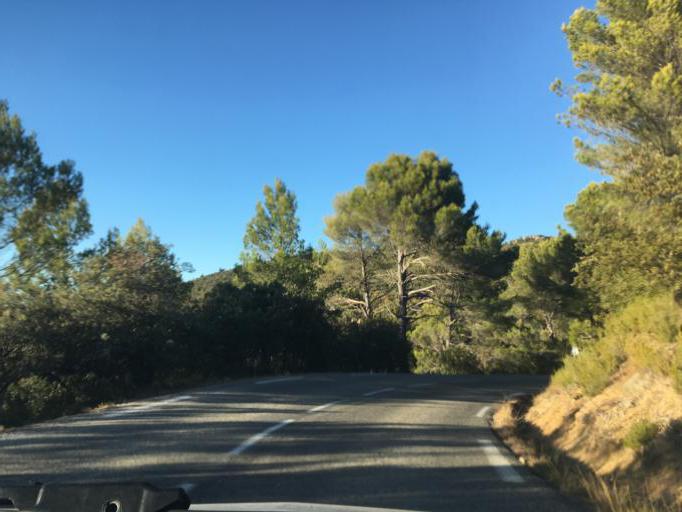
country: FR
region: Provence-Alpes-Cote d'Azur
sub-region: Departement du Var
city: Villecroze
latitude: 43.5950
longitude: 6.2835
